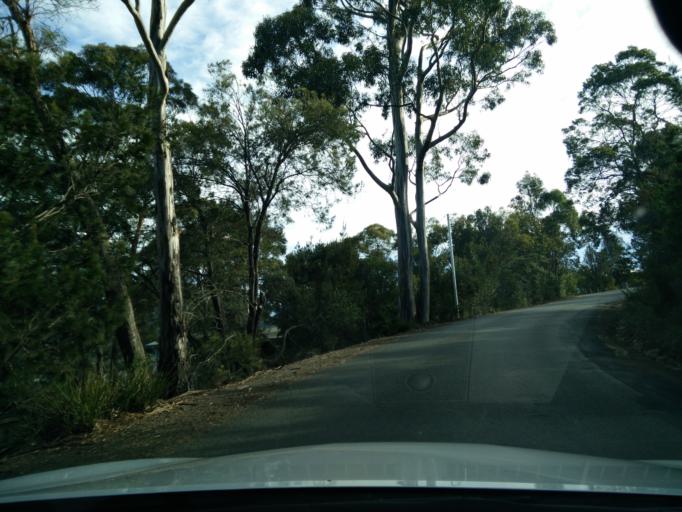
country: AU
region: Tasmania
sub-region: Break O'Day
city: St Helens
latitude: -42.1230
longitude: 148.2948
